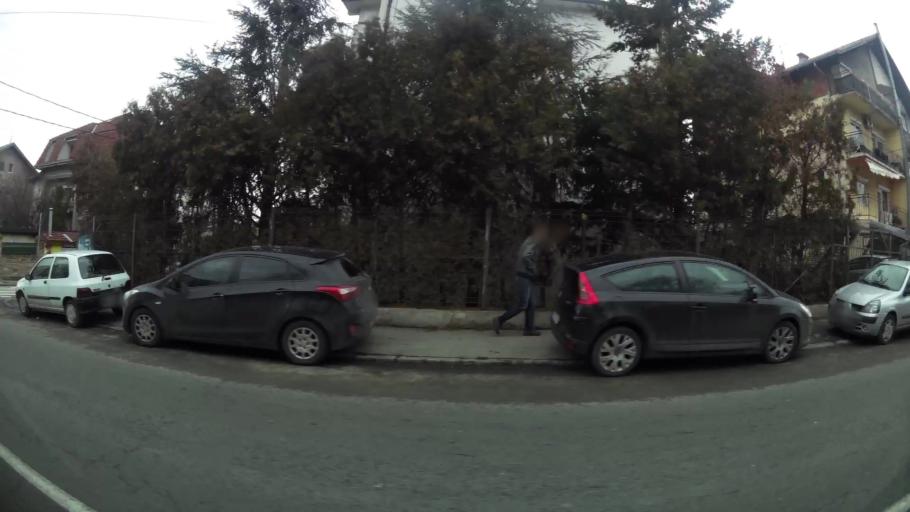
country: RS
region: Central Serbia
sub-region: Belgrade
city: Cukarica
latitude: 44.7612
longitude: 20.4081
